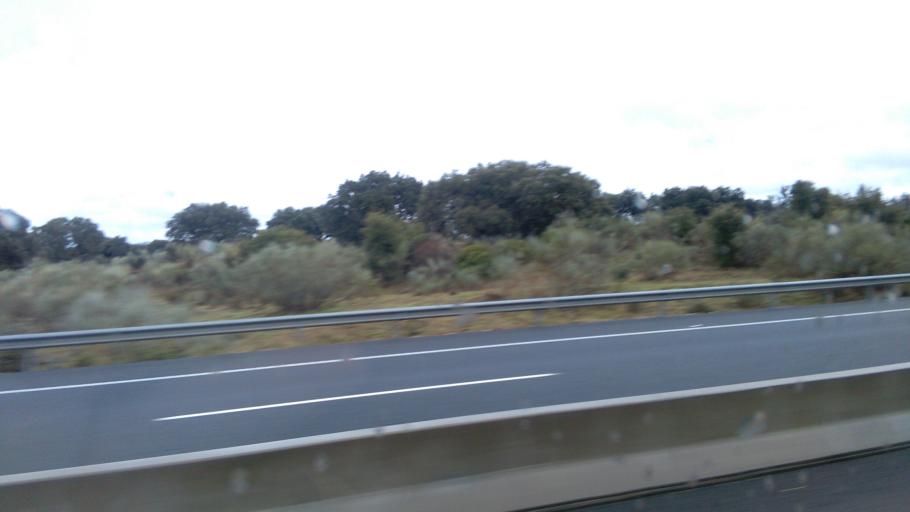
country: ES
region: Extremadura
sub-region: Provincia de Caceres
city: Casas de Miravete
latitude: 39.7663
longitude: -5.7350
